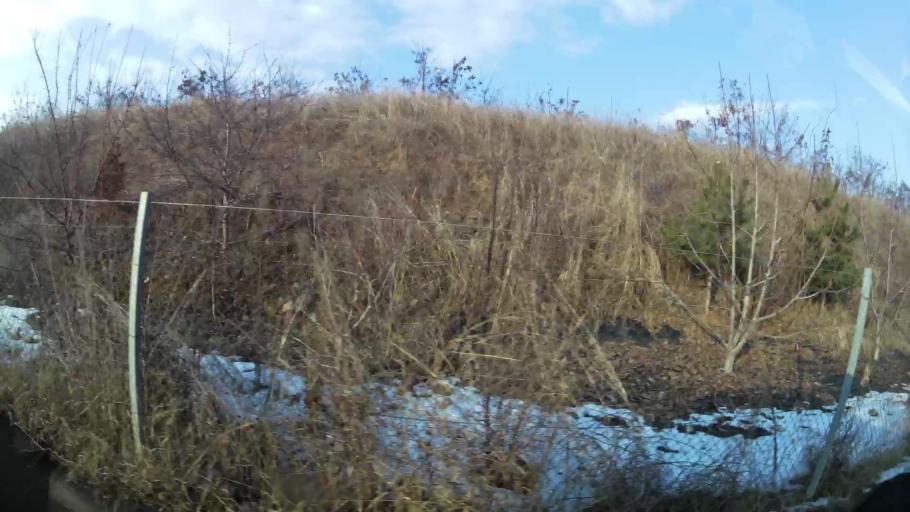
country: MK
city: Creshevo
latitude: 42.0337
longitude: 21.5202
